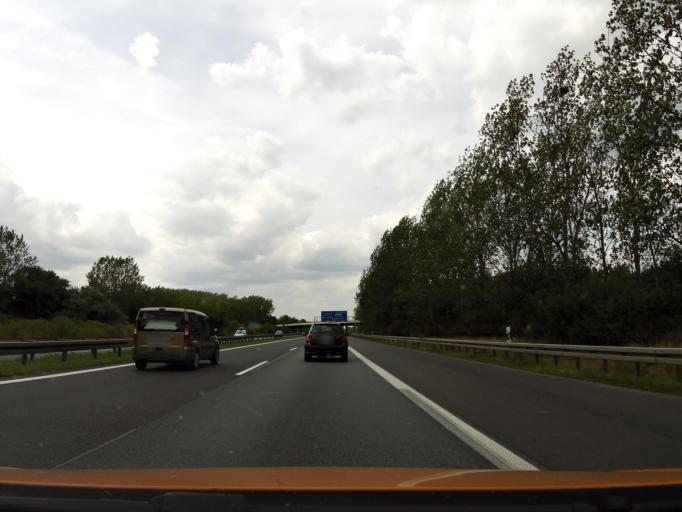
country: DE
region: Brandenburg
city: Leegebruch
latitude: 52.7004
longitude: 13.2274
